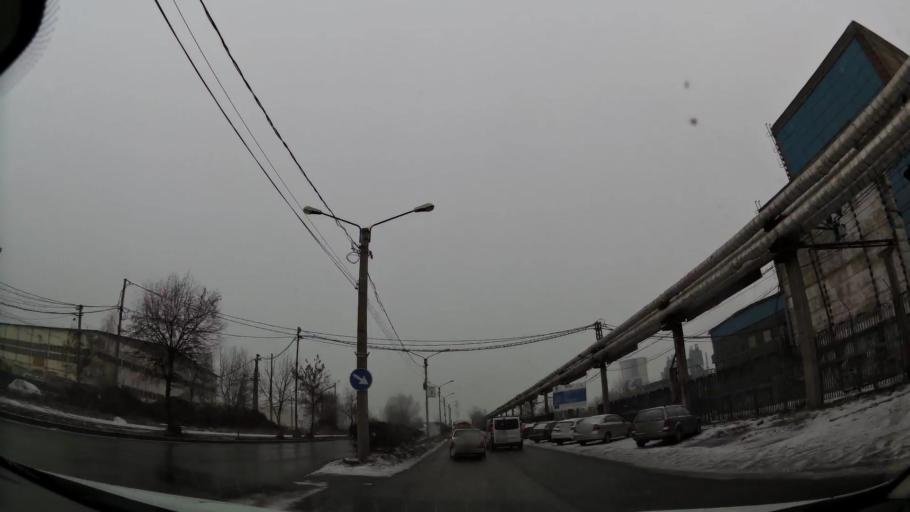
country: RO
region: Dambovita
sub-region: Municipiul Targoviste
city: Targoviste
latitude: 44.9097
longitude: 25.4600
